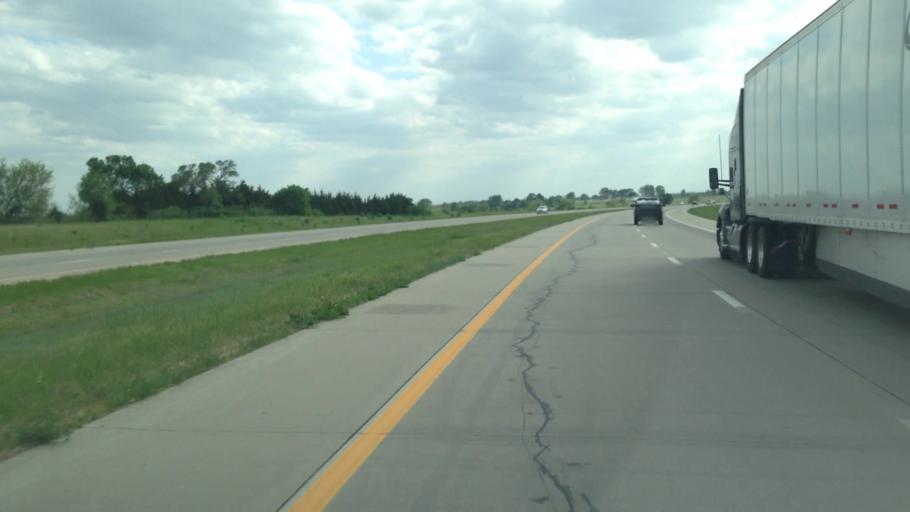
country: US
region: Kansas
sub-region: Franklin County
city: Ottawa
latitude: 38.5877
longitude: -95.2381
